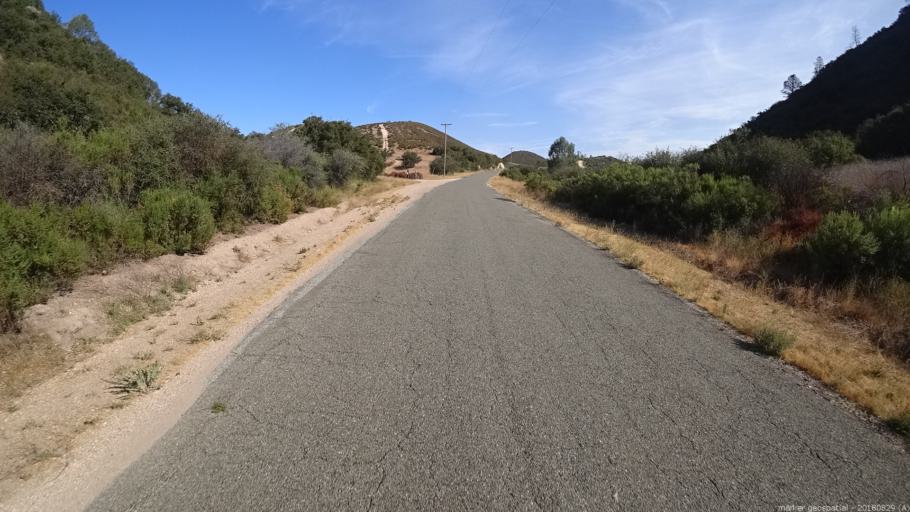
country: US
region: California
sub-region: Monterey County
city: King City
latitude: 36.0125
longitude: -121.0681
